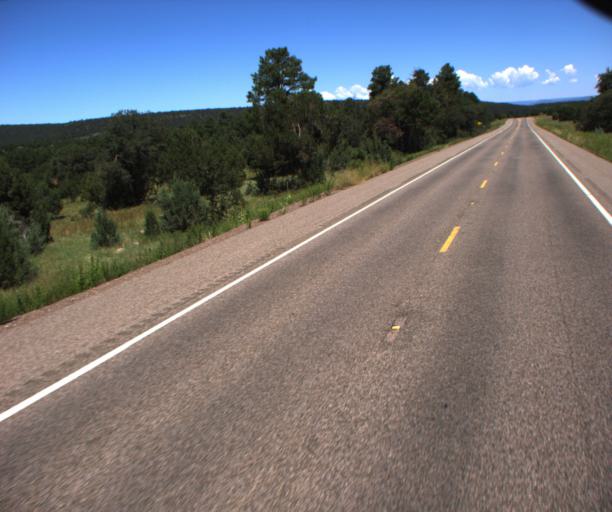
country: US
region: Arizona
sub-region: Gila County
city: San Carlos
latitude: 33.6689
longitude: -110.5724
